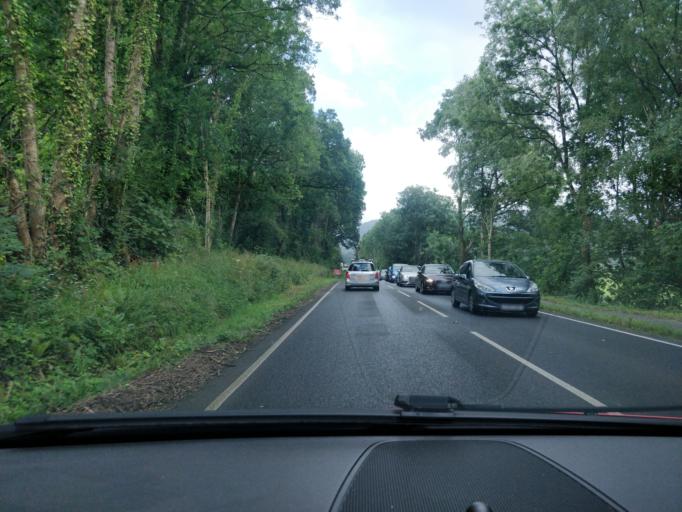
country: GB
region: Wales
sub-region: Conwy
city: Betws-y-Coed
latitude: 53.1066
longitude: -3.7852
